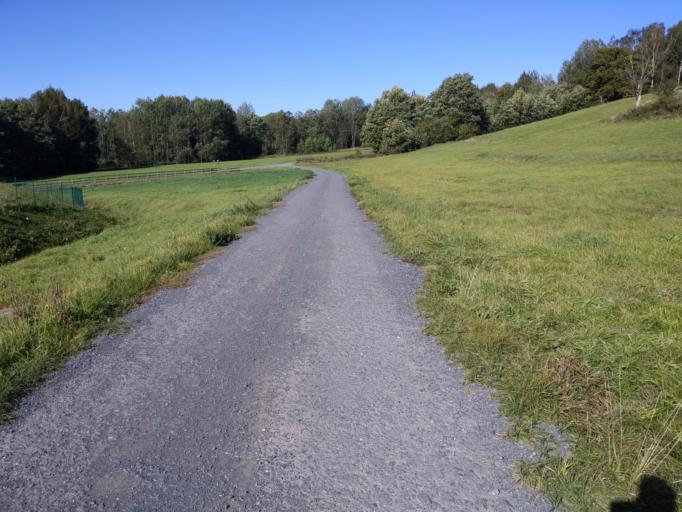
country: DE
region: Saxony
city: Schoneck
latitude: 50.3841
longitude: 12.3352
